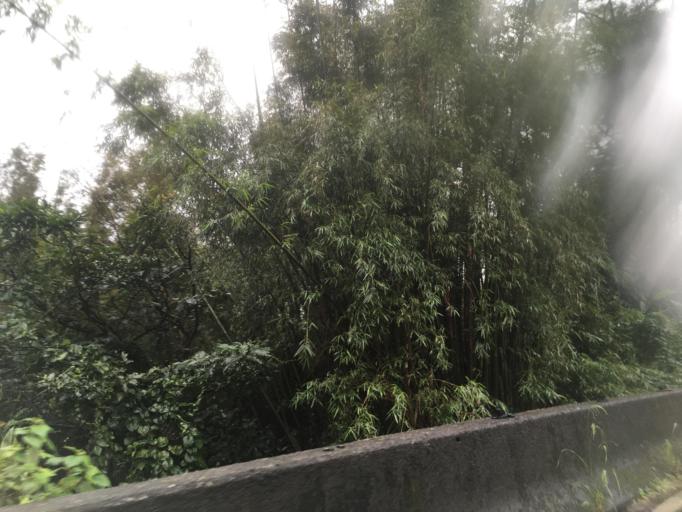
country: TW
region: Taiwan
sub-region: Keelung
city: Keelung
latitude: 25.0680
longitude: 121.9020
